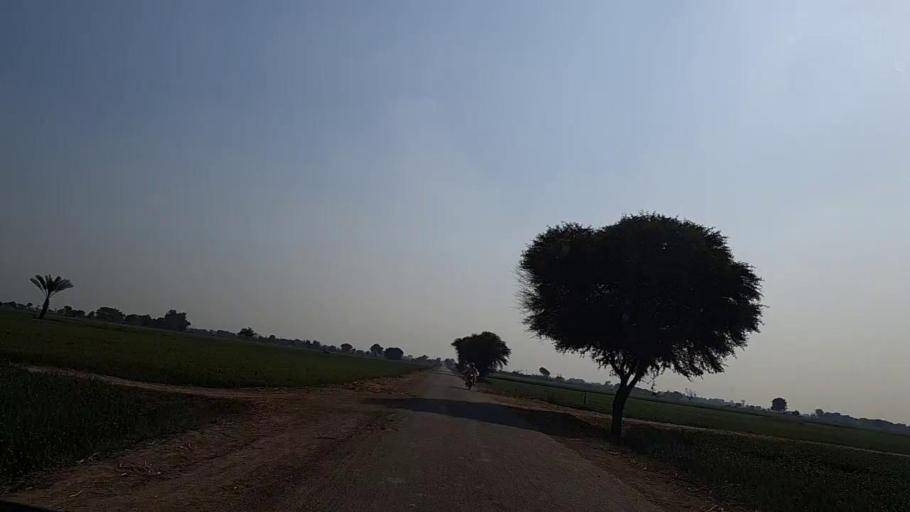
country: PK
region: Sindh
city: Sakrand
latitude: 26.0882
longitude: 68.2902
